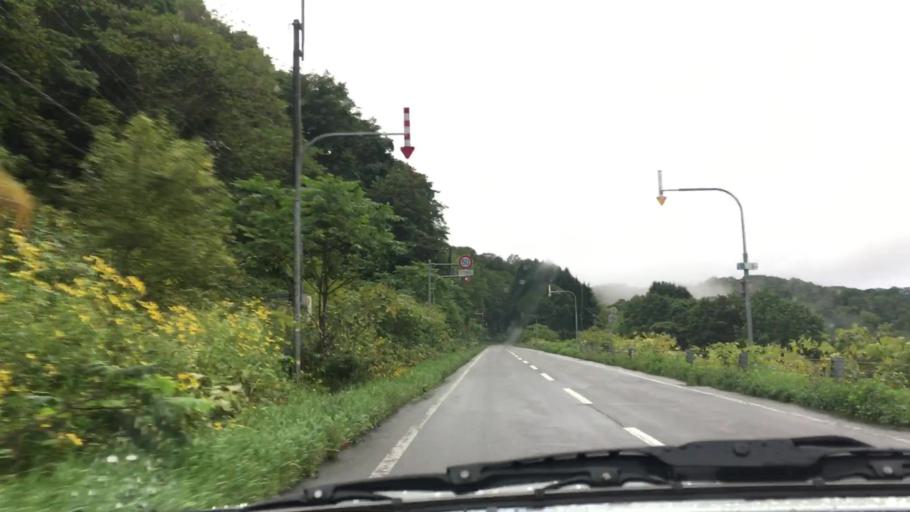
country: JP
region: Hokkaido
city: Niseko Town
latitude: 42.6322
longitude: 140.7265
